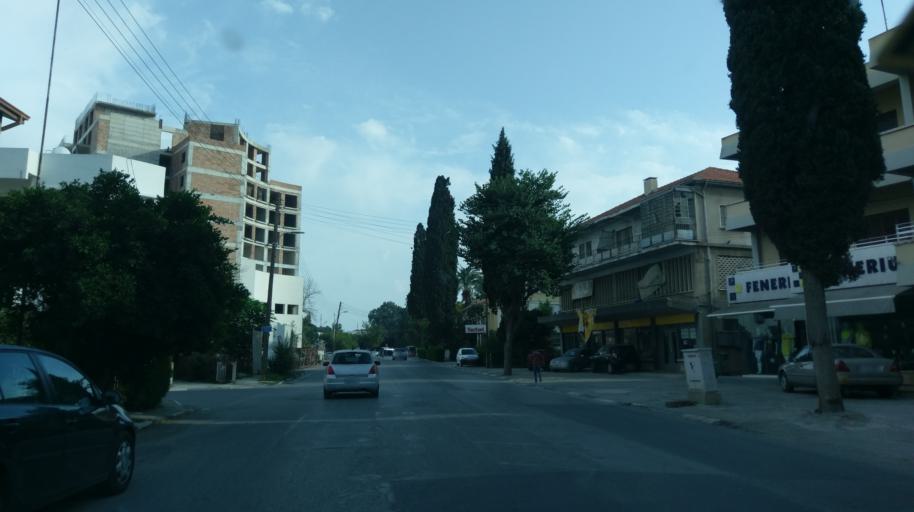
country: CY
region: Lefkosia
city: Nicosia
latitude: 35.1869
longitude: 33.3563
